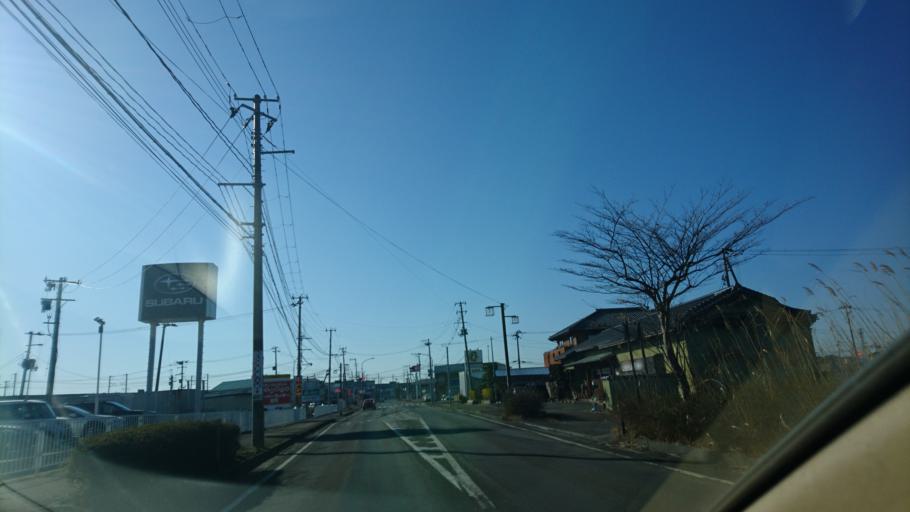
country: JP
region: Miyagi
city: Furukawa
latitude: 38.5960
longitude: 140.9765
